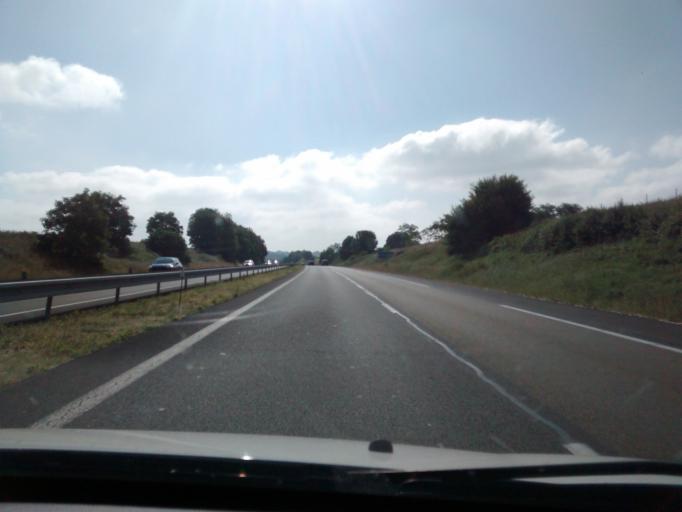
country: FR
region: Pays de la Loire
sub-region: Departement de la Sarthe
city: Loue
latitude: 48.0033
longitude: -0.2017
